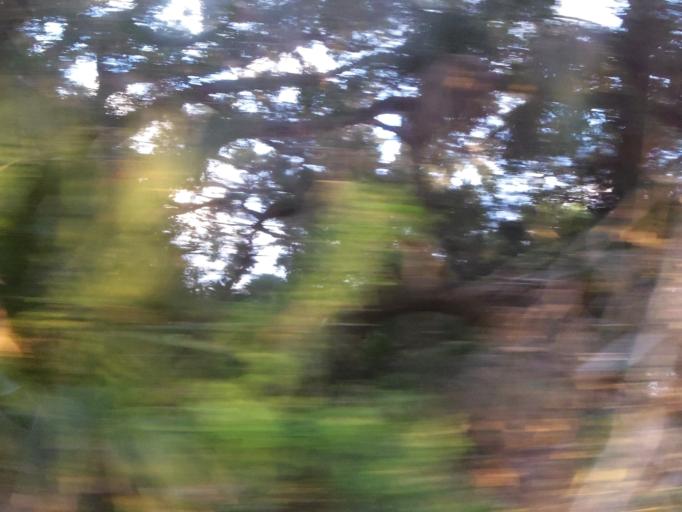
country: US
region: Florida
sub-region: Saint Johns County
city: Villano Beach
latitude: 29.9224
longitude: -81.2997
